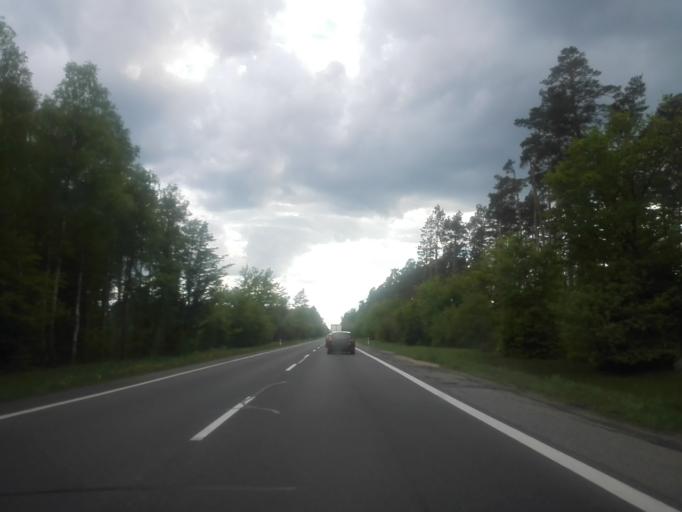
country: PL
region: Masovian Voivodeship
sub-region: Powiat ostrowski
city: Ostrow Mazowiecka
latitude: 52.7727
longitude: 21.8316
